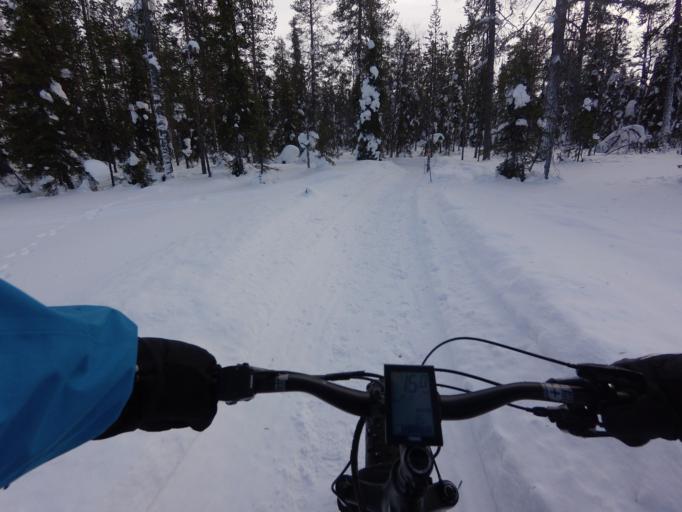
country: FI
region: Lapland
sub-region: Tunturi-Lappi
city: Kolari
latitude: 67.6000
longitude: 24.2156
